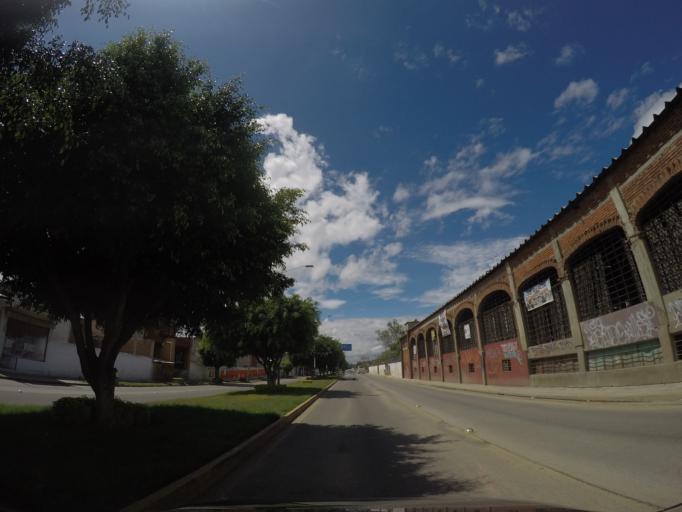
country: MX
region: Oaxaca
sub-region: Santa Cruz Xoxocotlan
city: Santa Cruz Xoxocotlan
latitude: 17.0407
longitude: -96.7291
